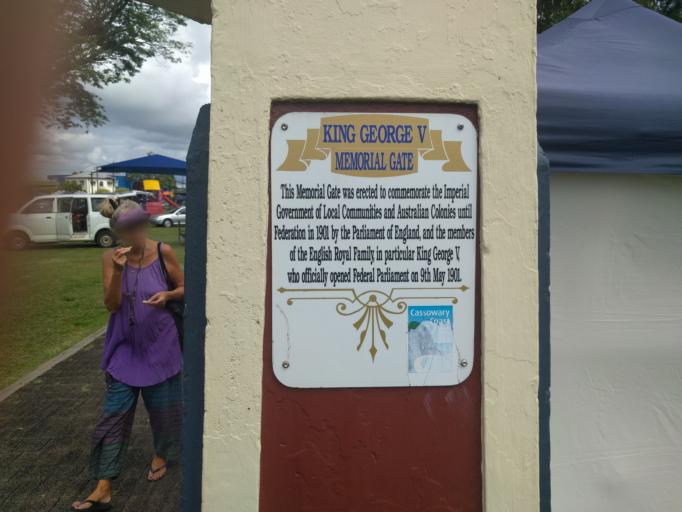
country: AU
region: Queensland
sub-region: Cassowary Coast
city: Innisfail
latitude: -17.5244
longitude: 146.0282
